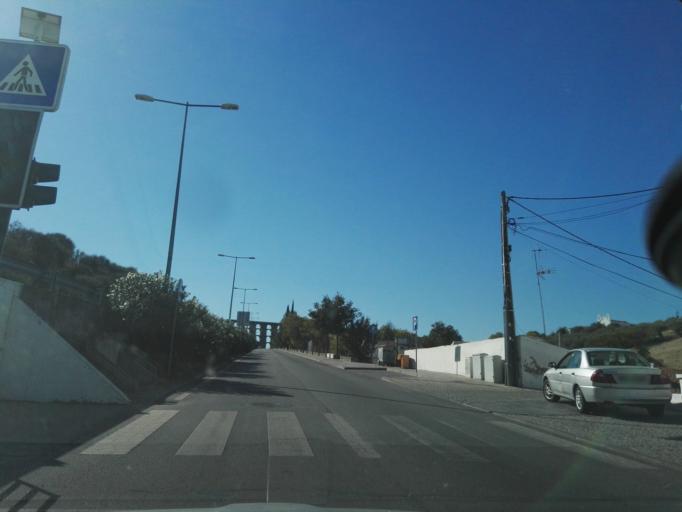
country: PT
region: Portalegre
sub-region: Elvas
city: Elvas
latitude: 38.8823
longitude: -7.1709
